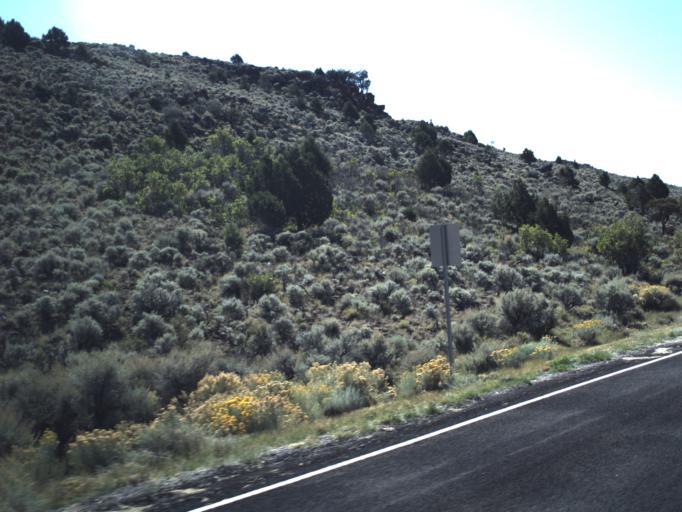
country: US
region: Utah
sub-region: Wayne County
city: Loa
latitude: 38.4752
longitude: -111.8308
